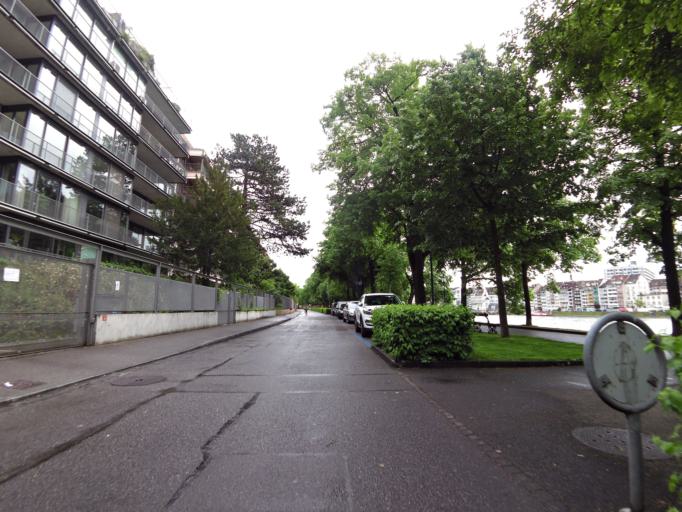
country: CH
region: Basel-City
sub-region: Basel-Stadt
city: Basel
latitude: 47.5652
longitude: 7.5872
